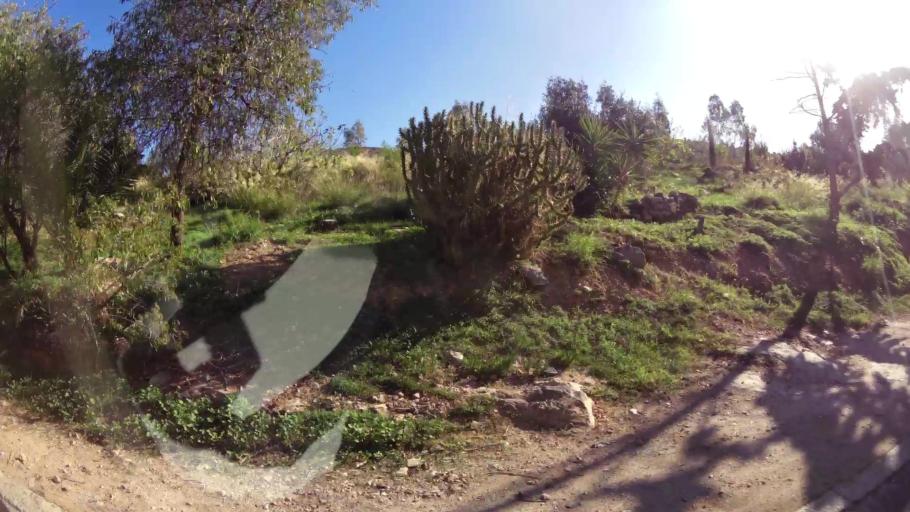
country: GR
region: Attica
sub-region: Nomarchia Athinas
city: Glyfada
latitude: 37.8619
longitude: 23.7720
